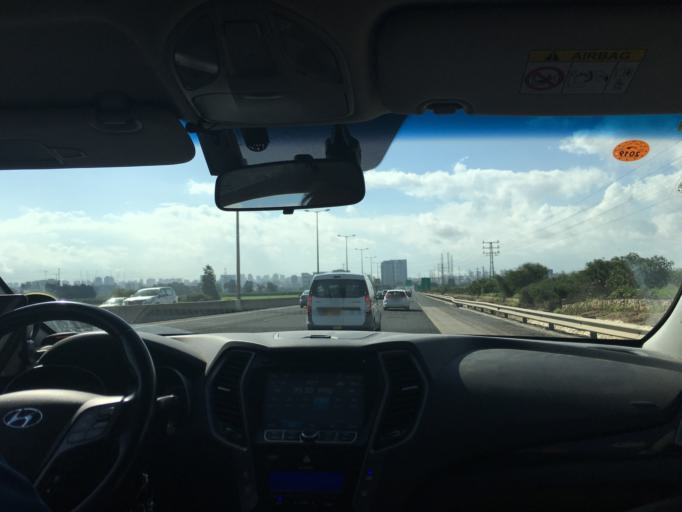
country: IL
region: Tel Aviv
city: Ramat HaSharon
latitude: 32.1164
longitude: 34.8513
